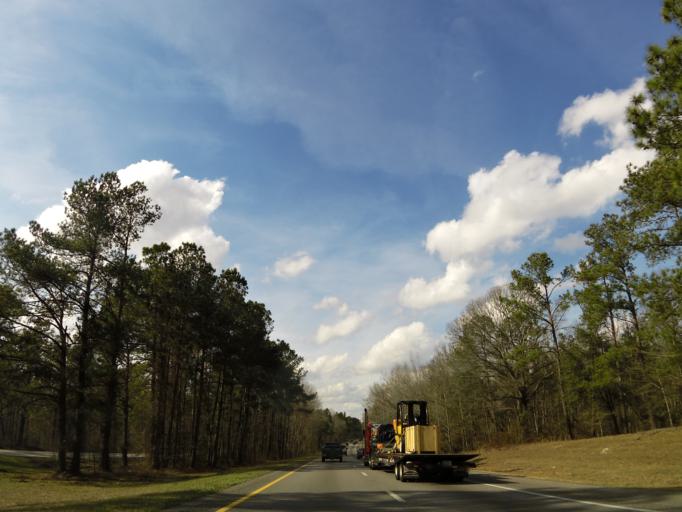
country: US
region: South Carolina
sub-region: Dorchester County
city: Ridgeville
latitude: 33.1557
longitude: -80.3477
